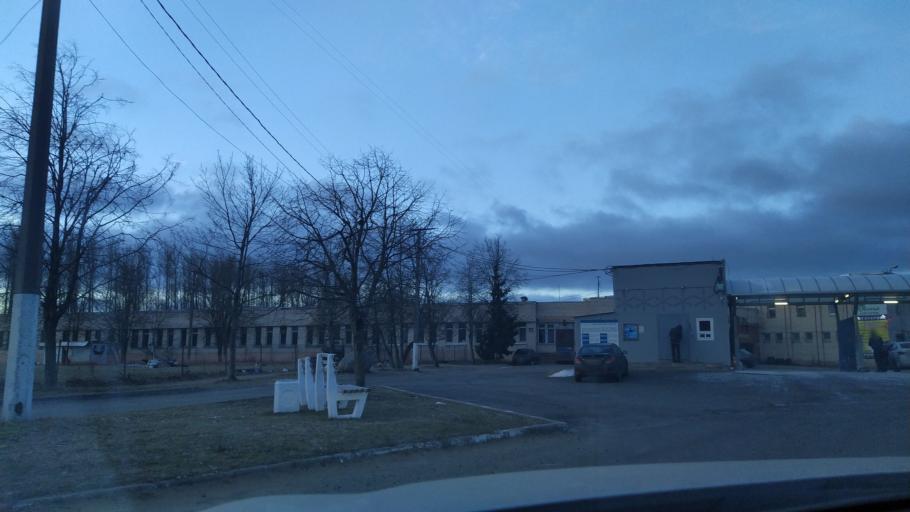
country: RU
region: St.-Petersburg
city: Pushkin
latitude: 59.7312
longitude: 30.3836
